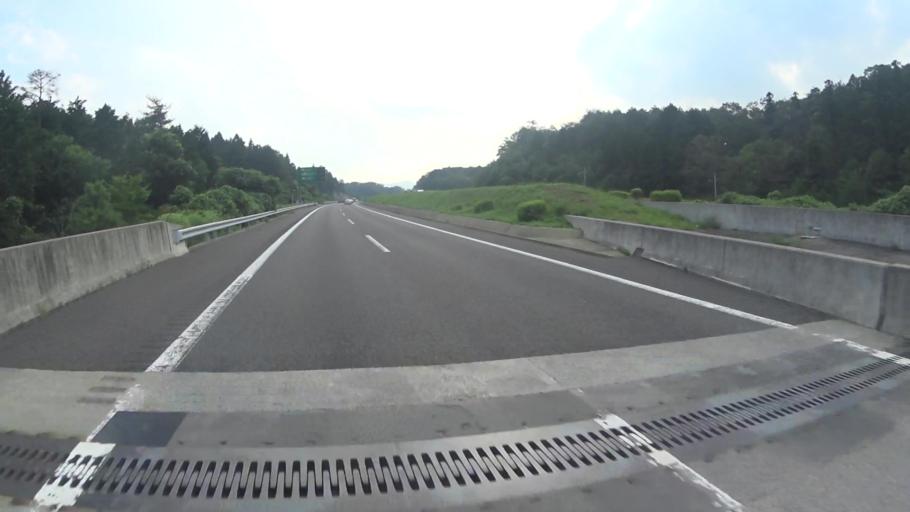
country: JP
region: Shiga Prefecture
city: Minakuchicho-matoba
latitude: 34.9167
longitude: 136.2116
